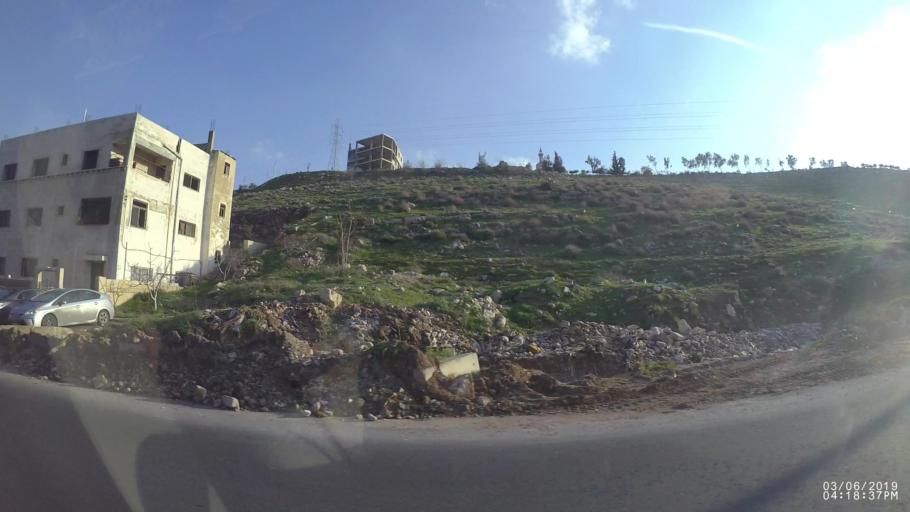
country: JO
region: Amman
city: Amman
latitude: 31.9816
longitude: 35.9659
